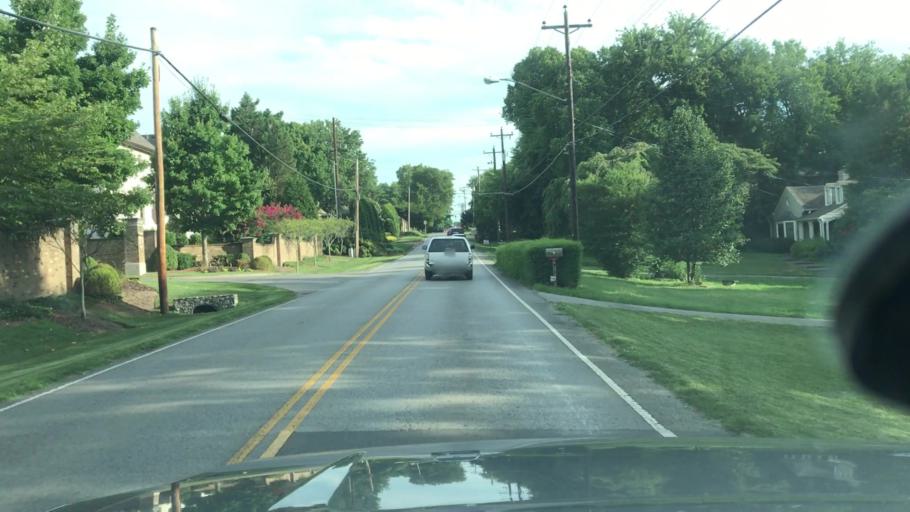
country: US
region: Tennessee
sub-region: Davidson County
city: Belle Meade
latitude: 36.1121
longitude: -86.8371
